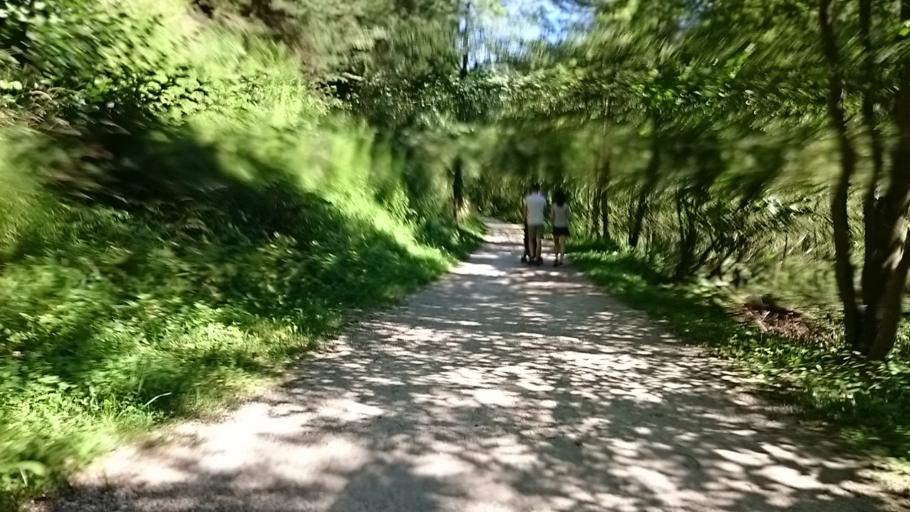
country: IT
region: Trentino-Alto Adige
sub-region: Bolzano
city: Riscone
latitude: 46.7864
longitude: 11.9526
